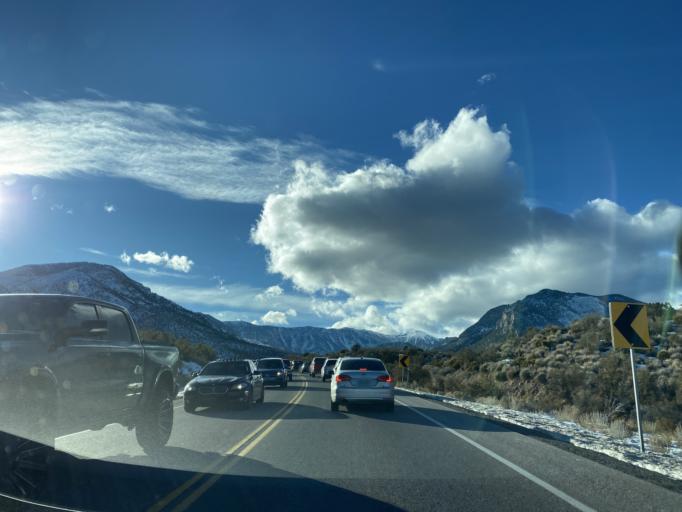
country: US
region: Nevada
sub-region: Clark County
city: Summerlin South
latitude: 36.2710
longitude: -115.5571
